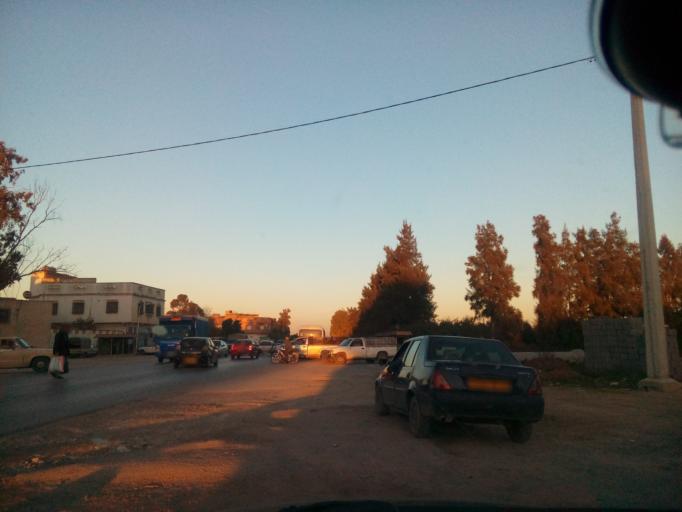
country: DZ
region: Relizane
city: Relizane
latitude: 35.7201
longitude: 0.3610
